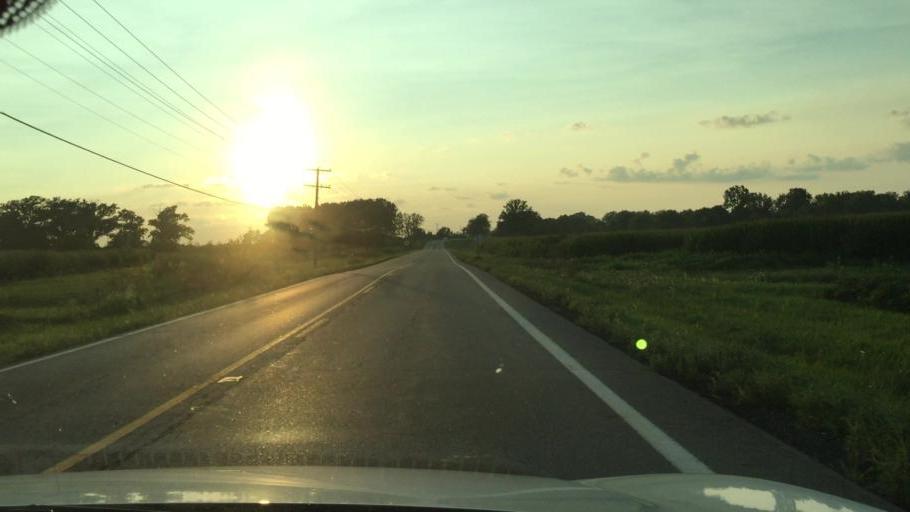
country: US
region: Ohio
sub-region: Madison County
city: Choctaw Lake
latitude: 39.9780
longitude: -83.3876
